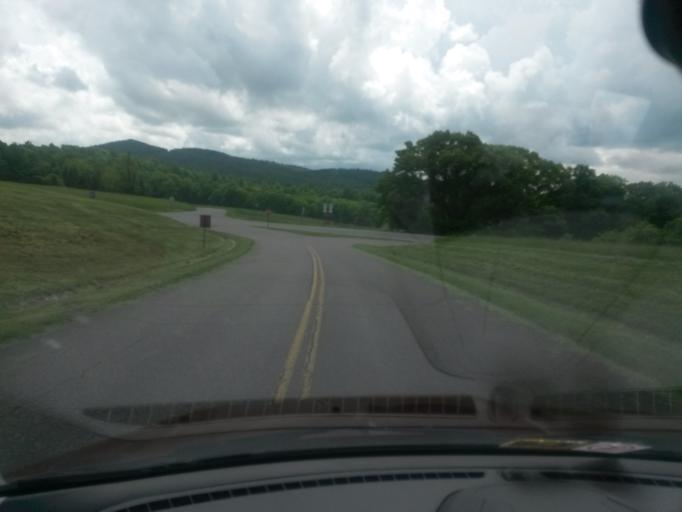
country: US
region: Virginia
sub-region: Floyd County
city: Floyd
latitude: 36.8431
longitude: -80.3211
